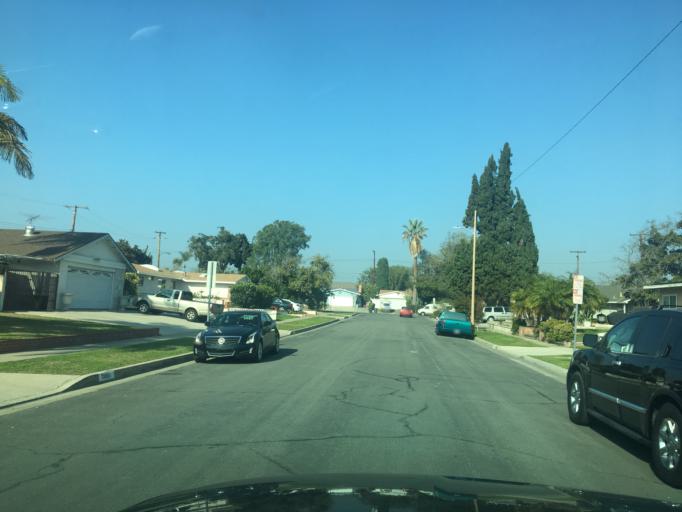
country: US
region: California
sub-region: Orange County
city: Tustin
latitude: 33.7356
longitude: -117.8288
